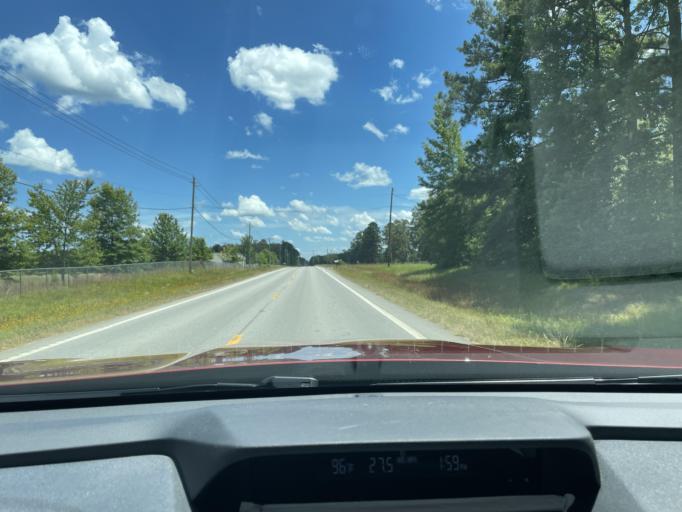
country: US
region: Arkansas
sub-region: Drew County
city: Monticello
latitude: 33.6198
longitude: -91.7483
